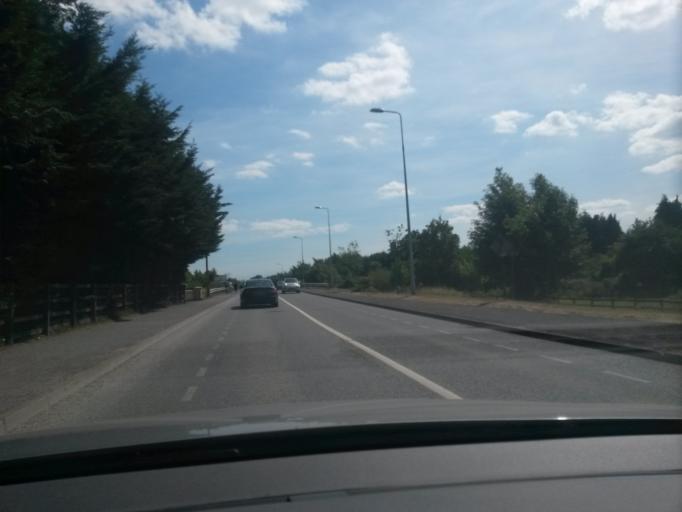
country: IE
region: Leinster
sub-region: Kildare
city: Sallins
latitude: 53.2418
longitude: -6.6655
